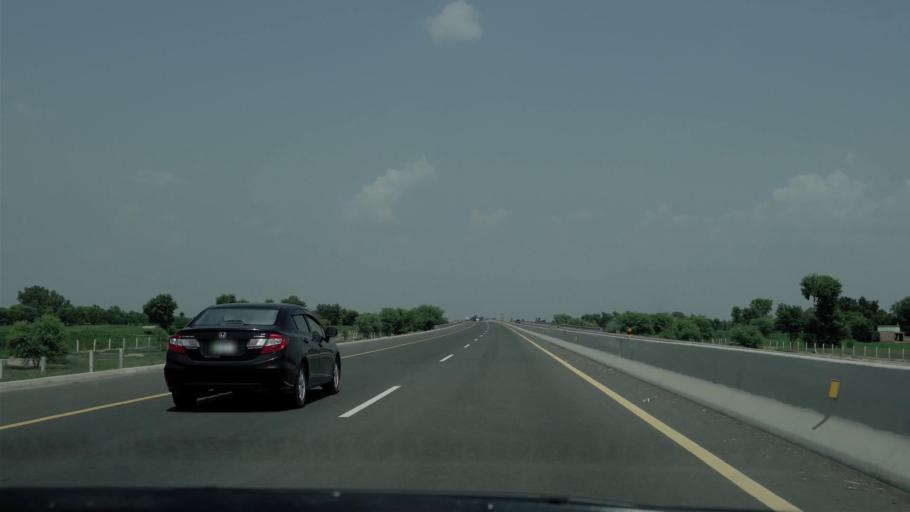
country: PK
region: Punjab
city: Gojra
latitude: 31.1897
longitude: 72.6483
